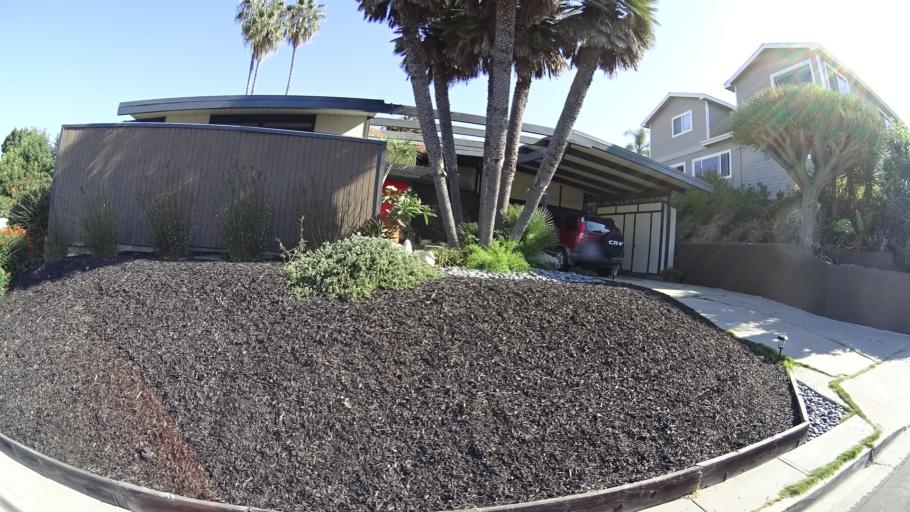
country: US
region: California
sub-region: Orange County
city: San Clemente
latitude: 33.4323
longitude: -117.6098
